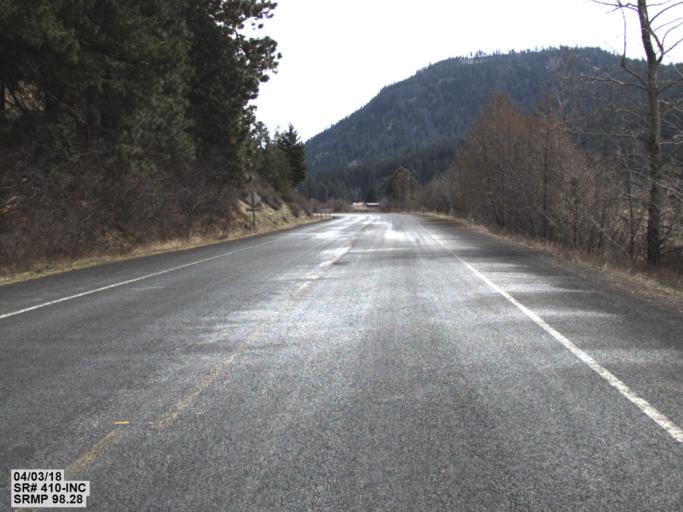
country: US
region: Washington
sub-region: Kittitas County
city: Cle Elum
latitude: 46.9173
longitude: -121.0420
